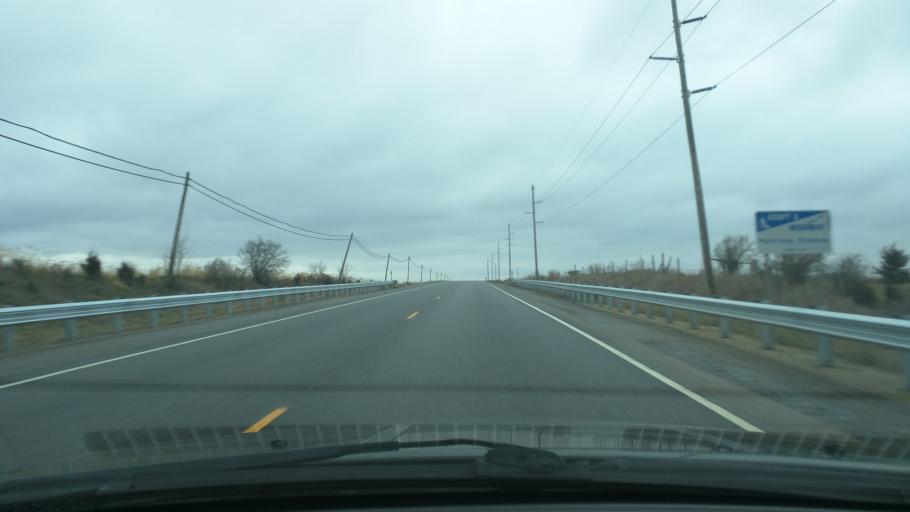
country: US
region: Minnesota
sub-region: Dakota County
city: Hastings
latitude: 44.7385
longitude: -92.9297
